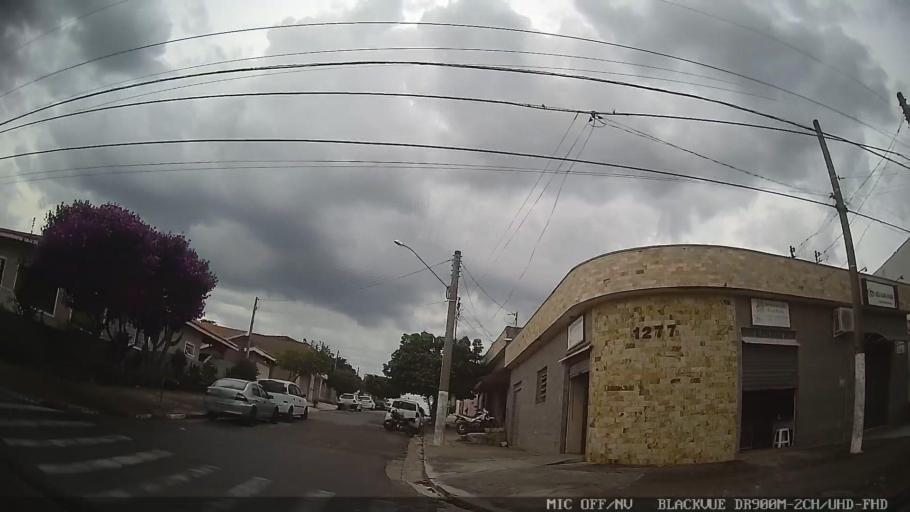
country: BR
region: Sao Paulo
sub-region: Atibaia
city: Atibaia
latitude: -23.1269
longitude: -46.5651
